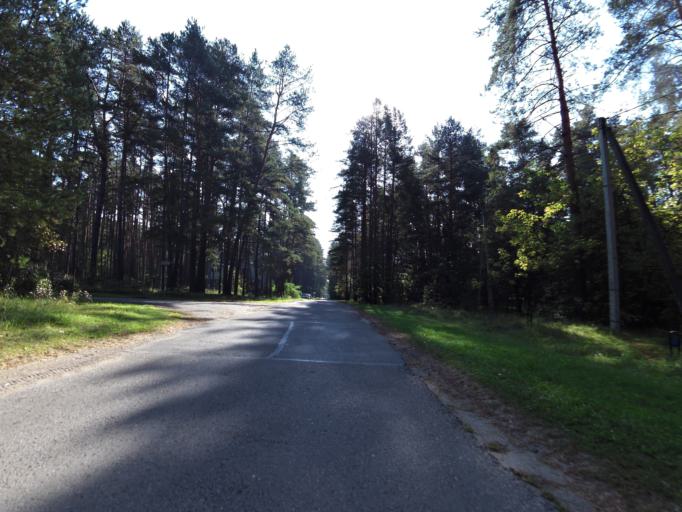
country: LT
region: Vilnius County
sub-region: Vilnius
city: Vilnius
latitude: 54.7332
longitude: 25.3105
